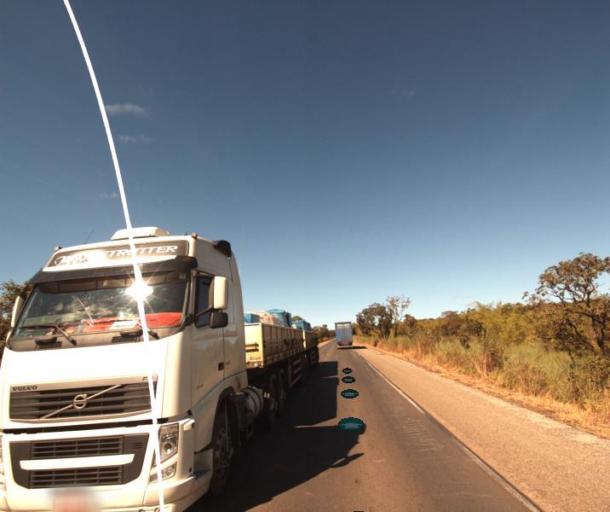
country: BR
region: Goias
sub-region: Itapaci
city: Itapaci
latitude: -14.9400
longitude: -49.3712
